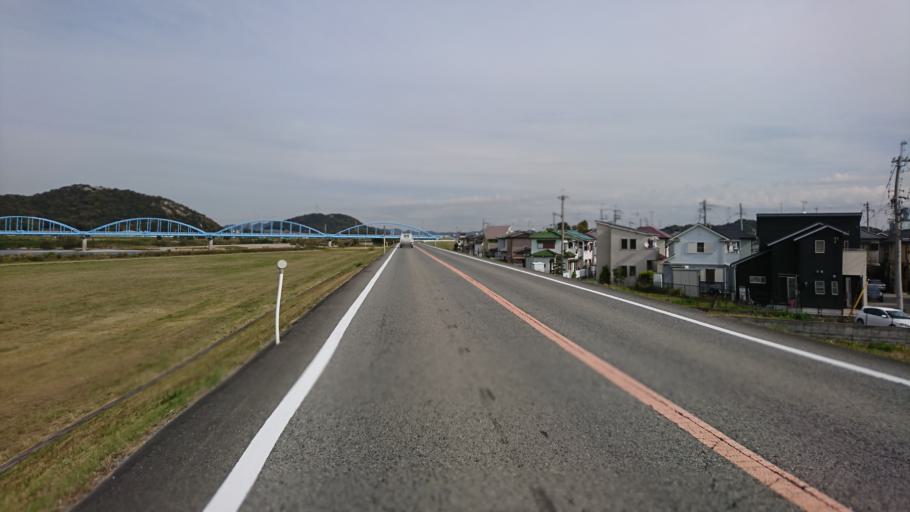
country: JP
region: Hyogo
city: Kakogawacho-honmachi
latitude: 34.7779
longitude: 134.8452
